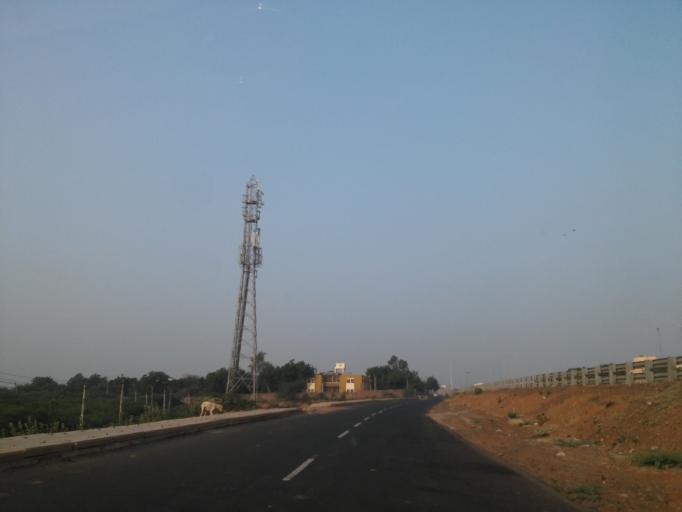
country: IN
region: Gujarat
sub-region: Kachchh
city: Bhachau
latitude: 23.2932
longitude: 70.3545
